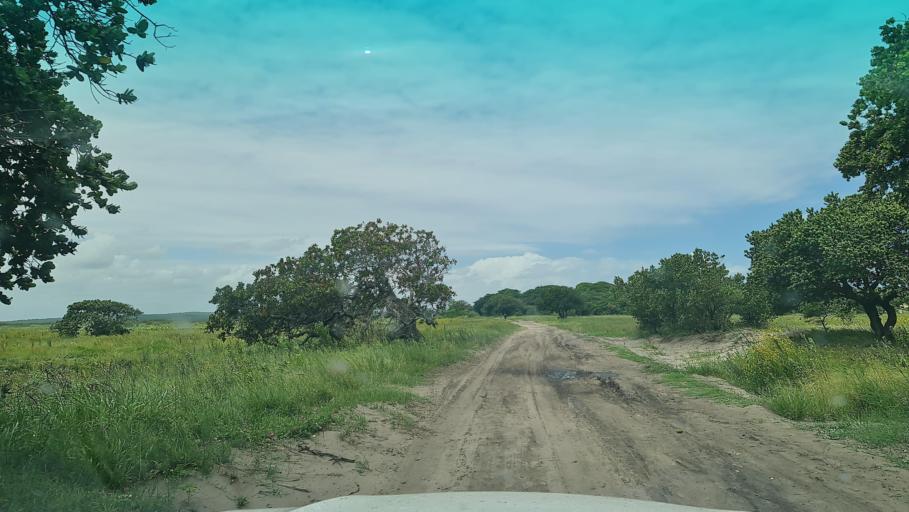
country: MZ
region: Maputo
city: Manhica
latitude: -25.5289
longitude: 32.8491
